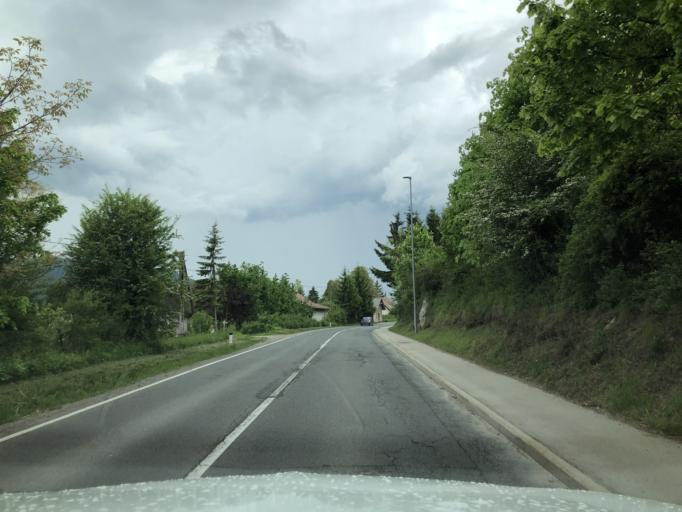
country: SI
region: Cerknica
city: Cerknica
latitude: 45.7953
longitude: 14.3441
